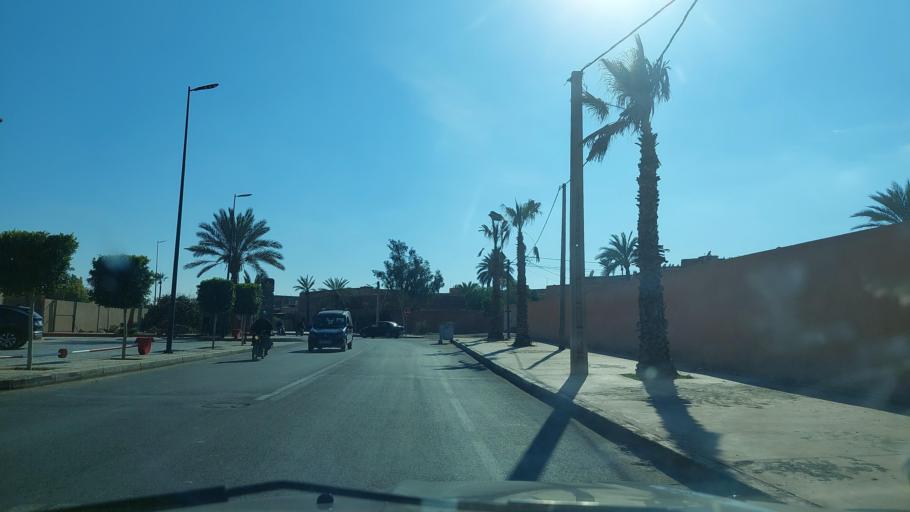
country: MA
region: Marrakech-Tensift-Al Haouz
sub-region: Marrakech
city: Marrakesh
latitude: 31.6617
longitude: -8.0624
